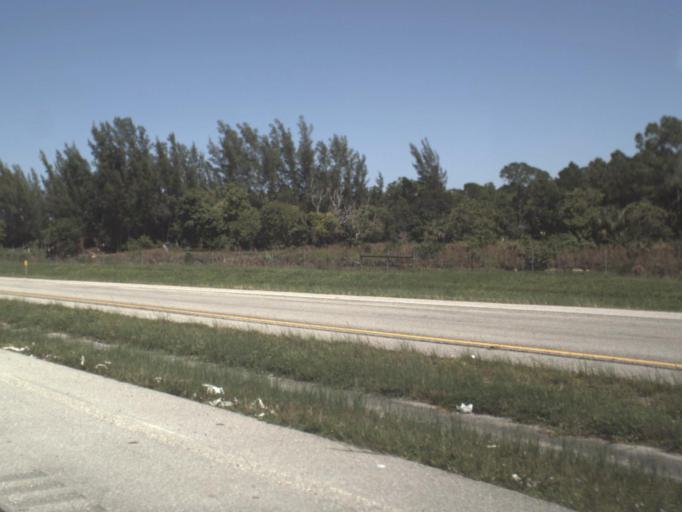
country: US
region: Florida
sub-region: Collier County
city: Golden Gate
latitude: 26.1797
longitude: -81.7353
